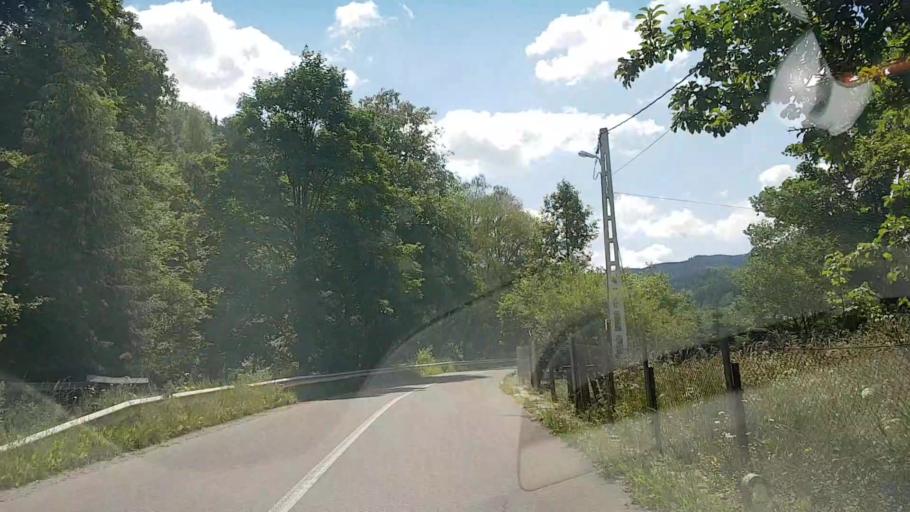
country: RO
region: Suceava
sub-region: Comuna Pojorata
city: Pojorata
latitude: 47.4929
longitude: 25.4845
